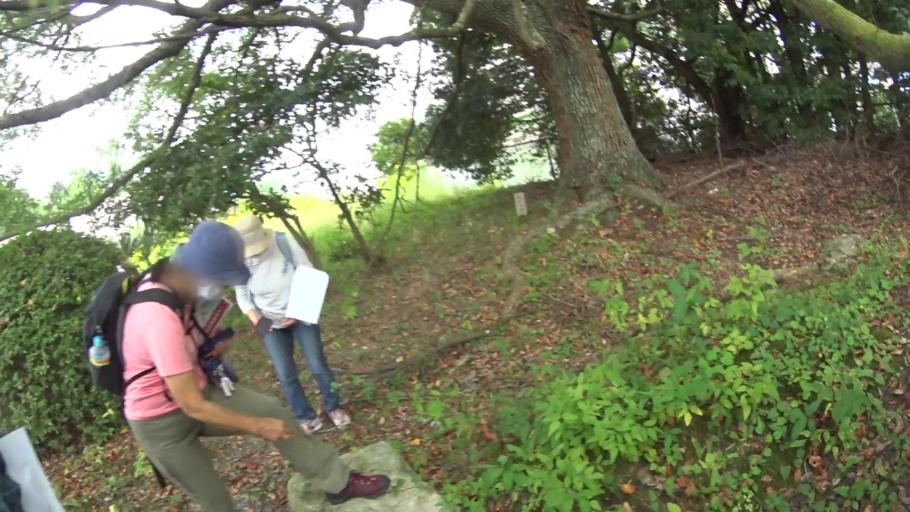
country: JP
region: Osaka
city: Kishiwada
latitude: 34.5088
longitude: 135.3414
